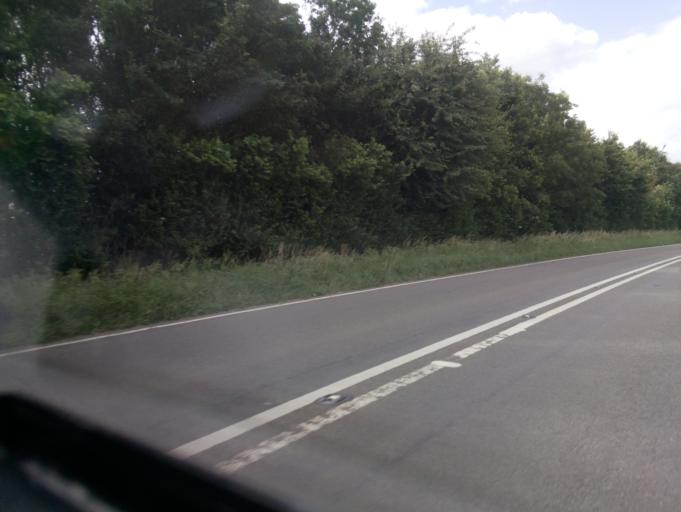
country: GB
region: England
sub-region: Leicestershire
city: Measham
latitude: 52.6655
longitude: -1.5389
